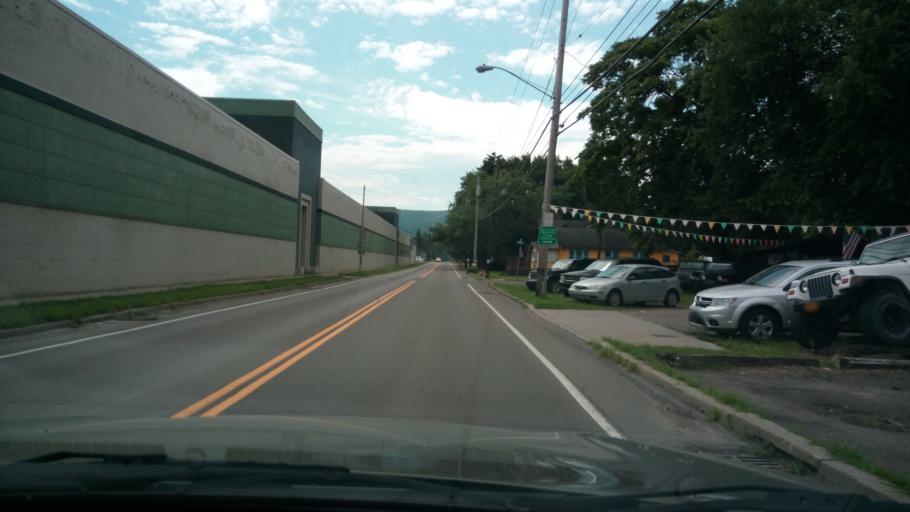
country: US
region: New York
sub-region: Chemung County
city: Southport
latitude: 42.0669
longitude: -76.7970
